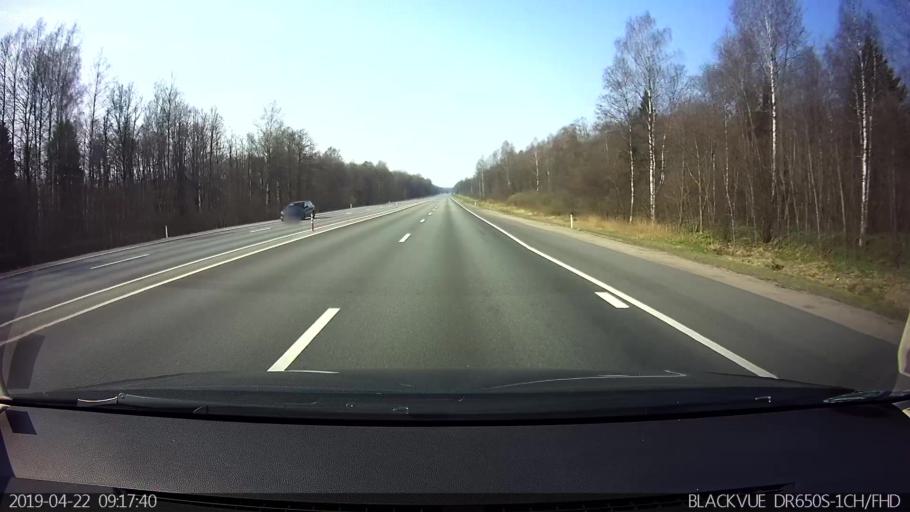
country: RU
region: Smolensk
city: Golynki
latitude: 54.7613
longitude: 31.5104
